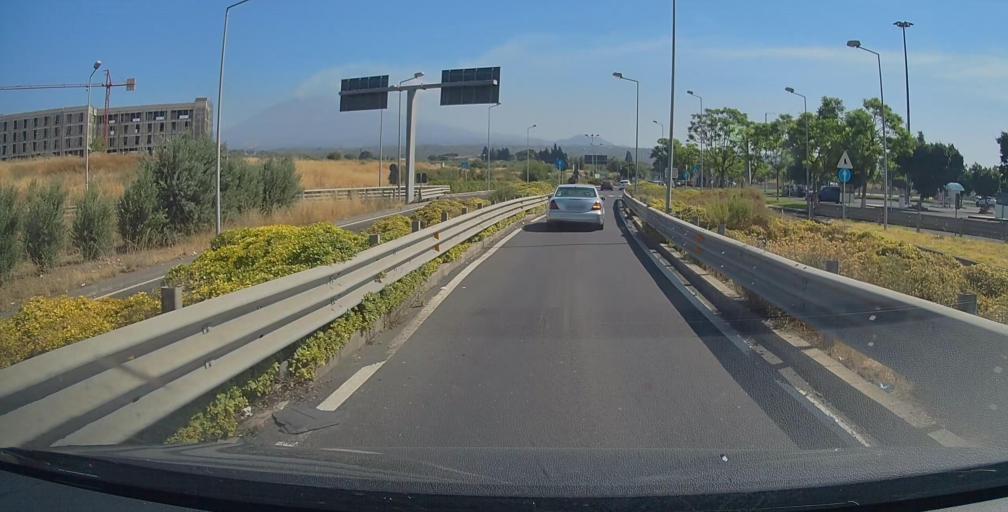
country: IT
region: Sicily
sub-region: Catania
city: Palazzolo
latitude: 37.5474
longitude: 14.9471
